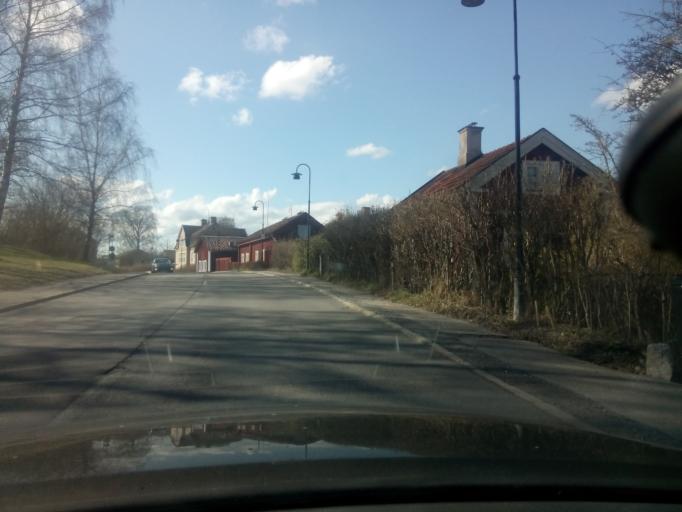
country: SE
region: Soedermanland
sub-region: Flens Kommun
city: Malmkoping
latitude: 59.1310
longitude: 16.7347
